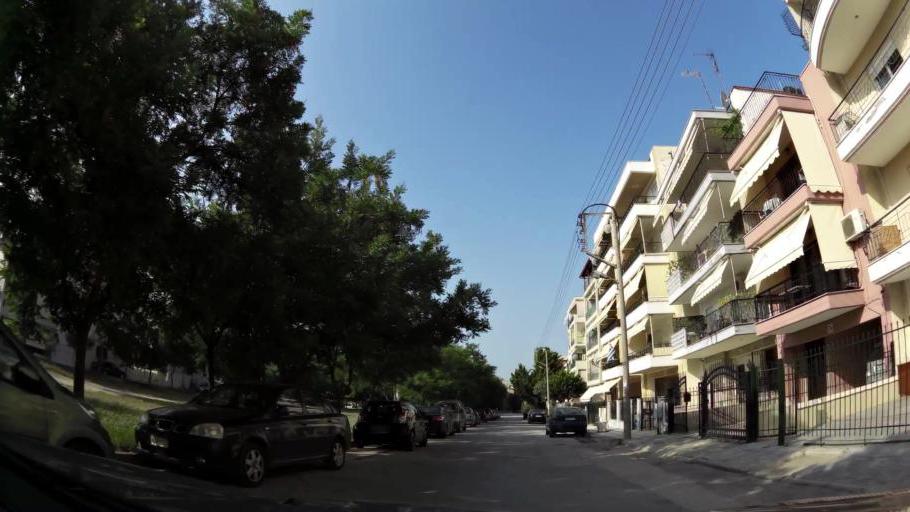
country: GR
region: Central Macedonia
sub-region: Nomos Thessalonikis
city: Evosmos
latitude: 40.6659
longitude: 22.9165
